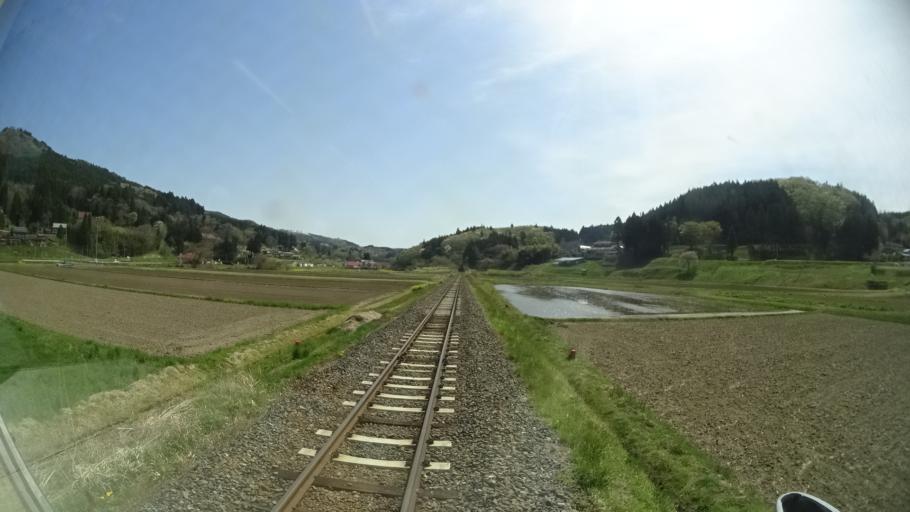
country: JP
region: Iwate
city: Ofunato
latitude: 38.9153
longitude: 141.4763
